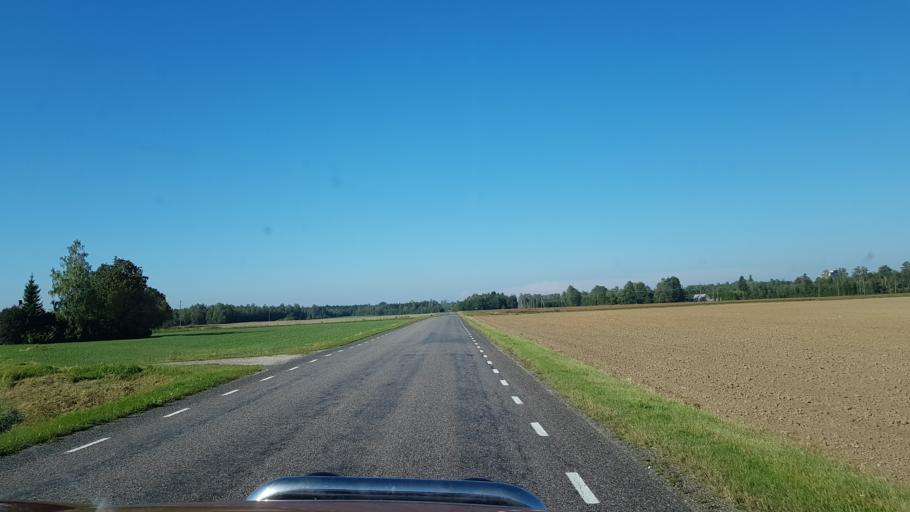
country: EE
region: Jogevamaa
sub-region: Jogeva linn
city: Jogeva
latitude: 58.6995
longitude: 26.3928
